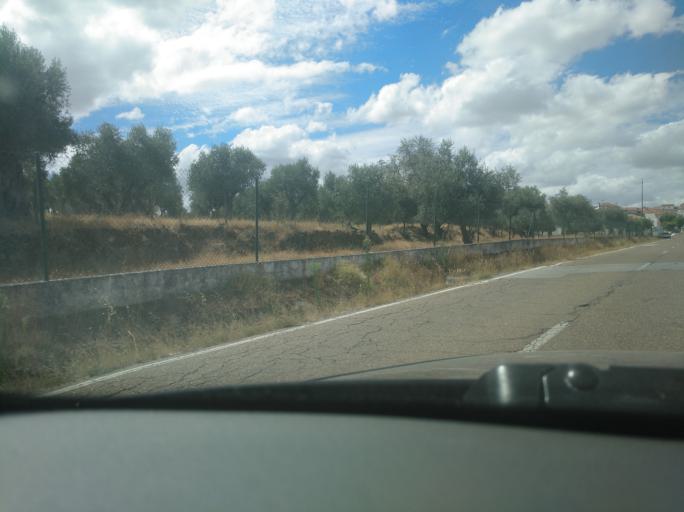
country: PT
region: Portalegre
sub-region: Arronches
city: Arronches
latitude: 39.0494
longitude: -7.4347
